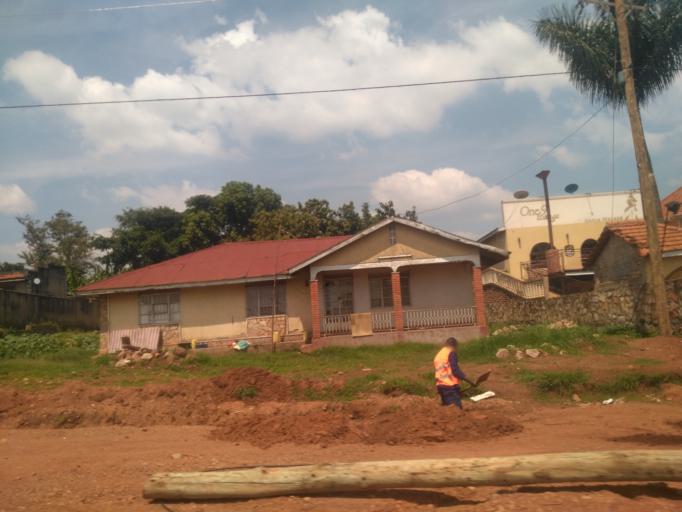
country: UG
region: Central Region
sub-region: Wakiso District
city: Entebbe
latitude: 0.0642
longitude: 32.4738
